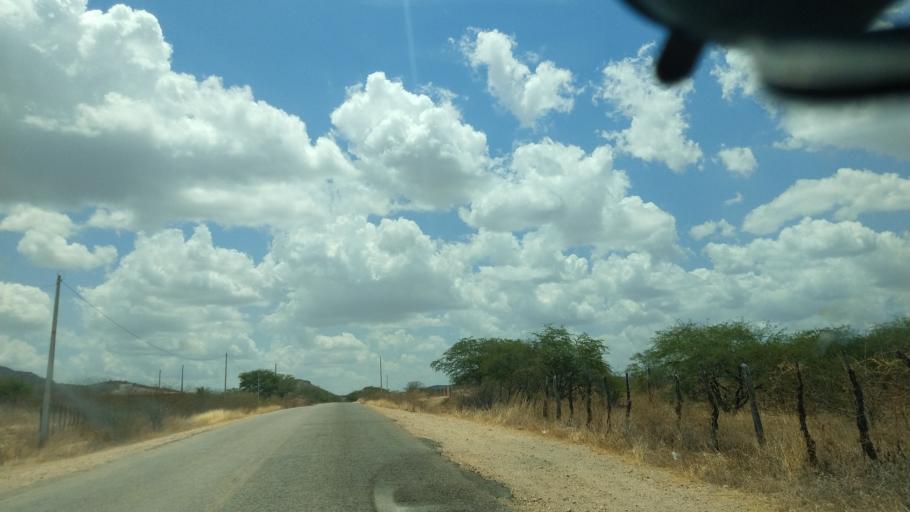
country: BR
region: Rio Grande do Norte
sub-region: Currais Novos
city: Currais Novos
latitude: -6.2741
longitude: -36.5448
